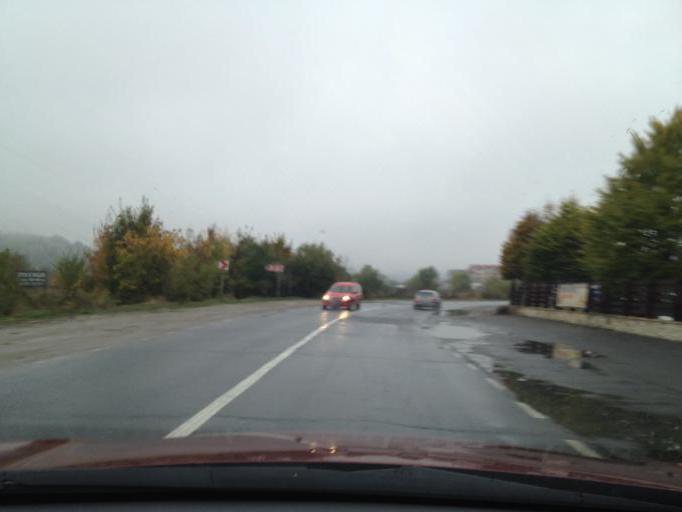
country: RO
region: Brasov
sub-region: Comuna Zarnesti
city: Tohanu Nou
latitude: 45.5416
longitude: 25.3800
